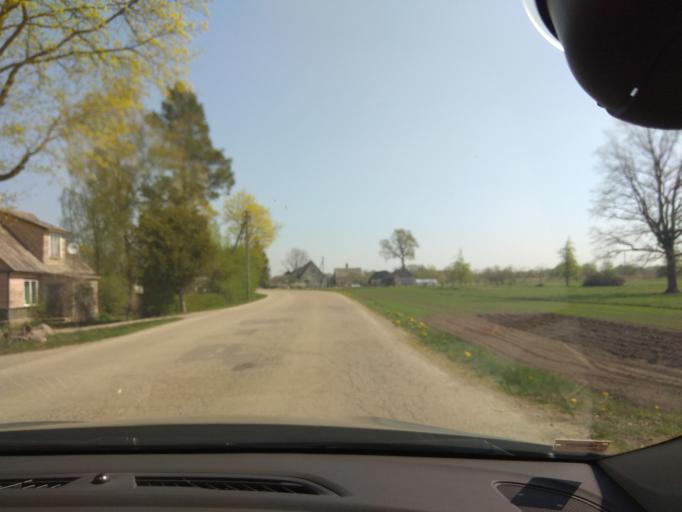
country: LT
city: Linkuva
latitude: 56.0258
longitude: 23.9551
